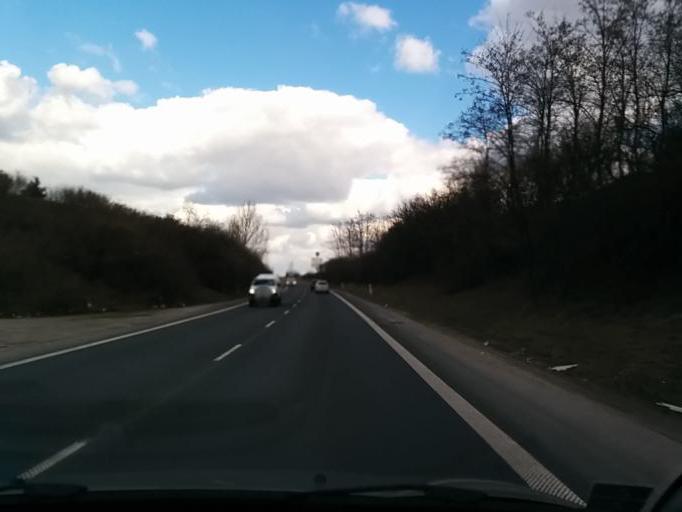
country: SK
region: Trnavsky
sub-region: Okres Trnava
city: Trnava
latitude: 48.3623
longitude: 17.6140
